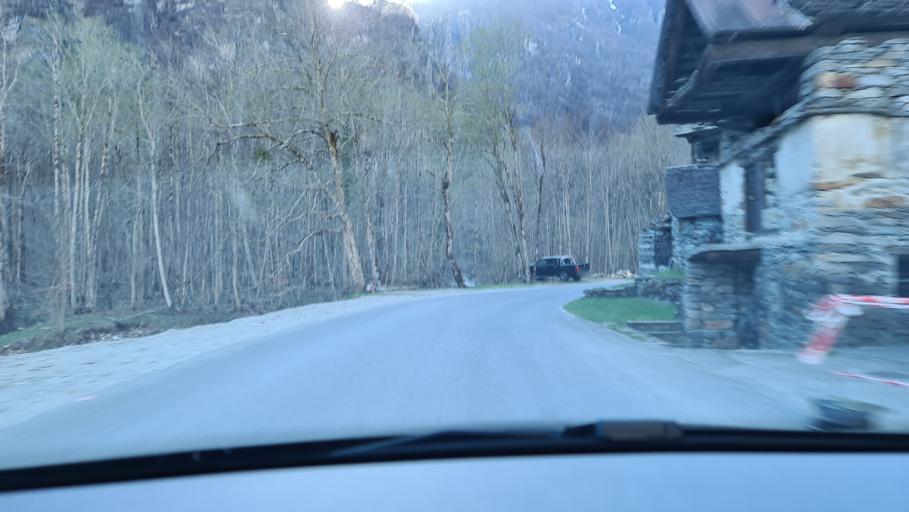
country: CH
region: Ticino
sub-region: Vallemaggia District
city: Cevio
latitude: 46.3707
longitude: 8.5570
